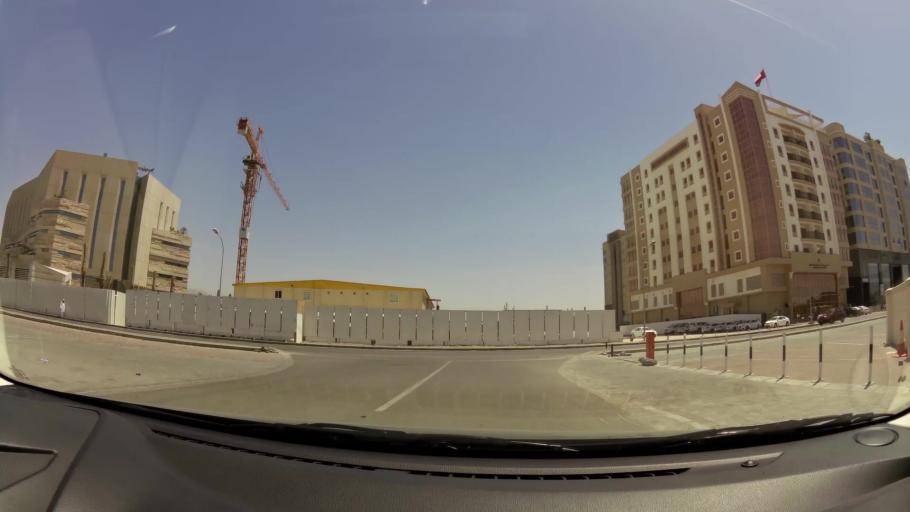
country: OM
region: Muhafazat Masqat
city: Bawshar
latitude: 23.5909
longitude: 58.3819
